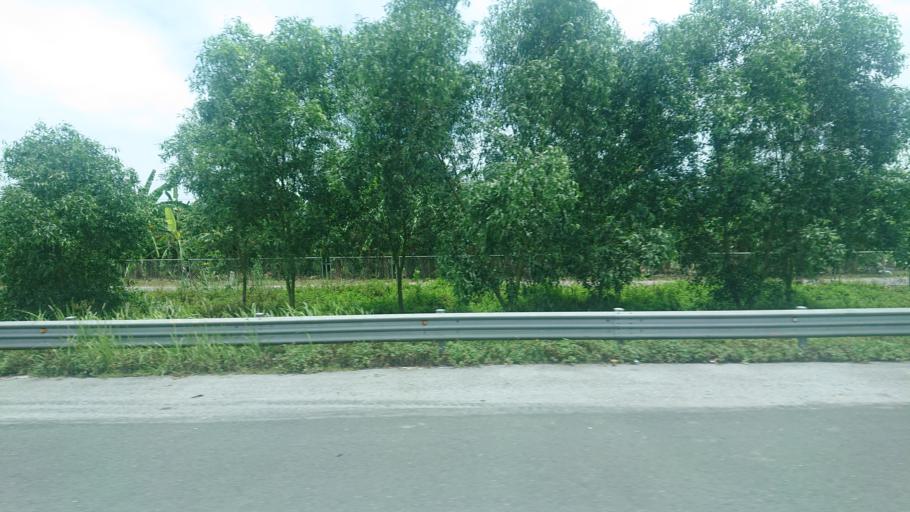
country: VN
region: Hai Phong
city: An Lao
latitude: 20.8163
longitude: 106.4900
